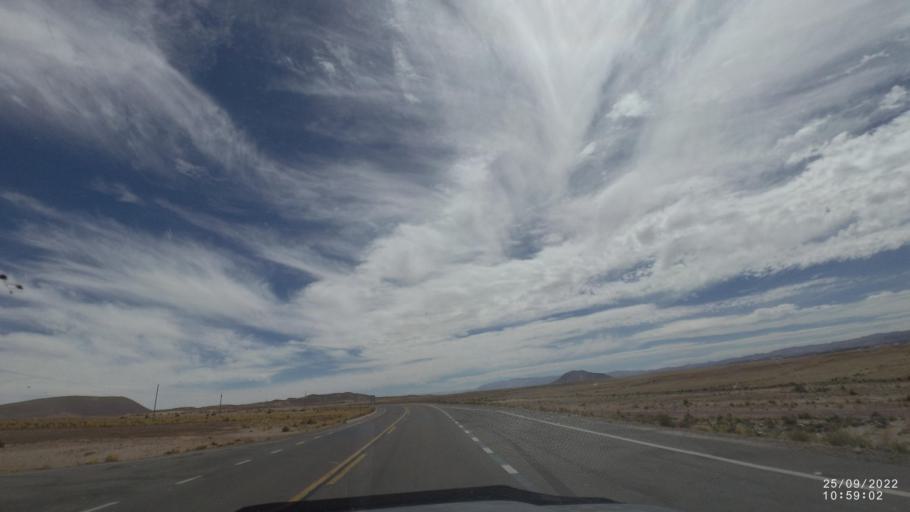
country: BO
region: Oruro
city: Challapata
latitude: -19.4554
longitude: -66.9092
